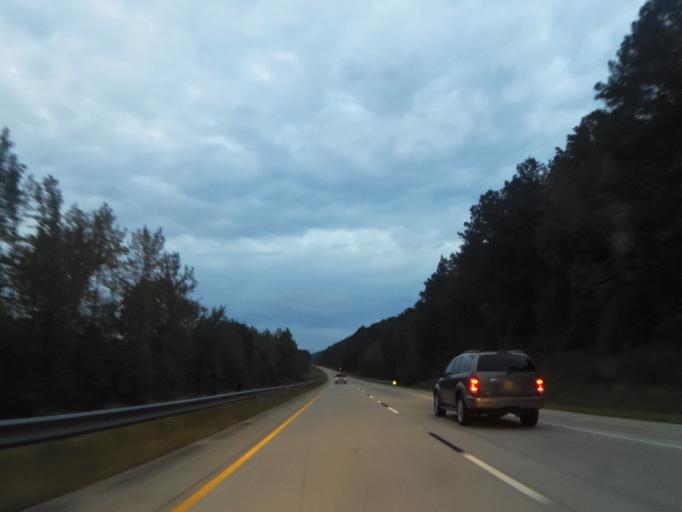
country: US
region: Alabama
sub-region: Etowah County
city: Gadsden
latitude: 34.1041
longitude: -85.9977
